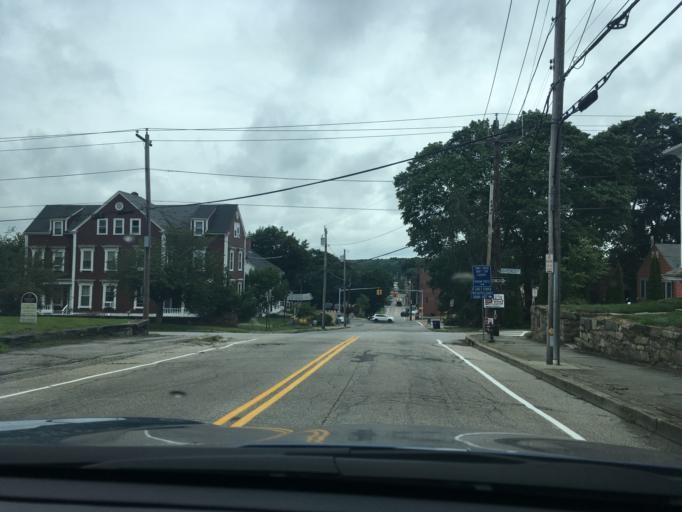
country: US
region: Rhode Island
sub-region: Kent County
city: East Greenwich
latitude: 41.6639
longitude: -71.4518
